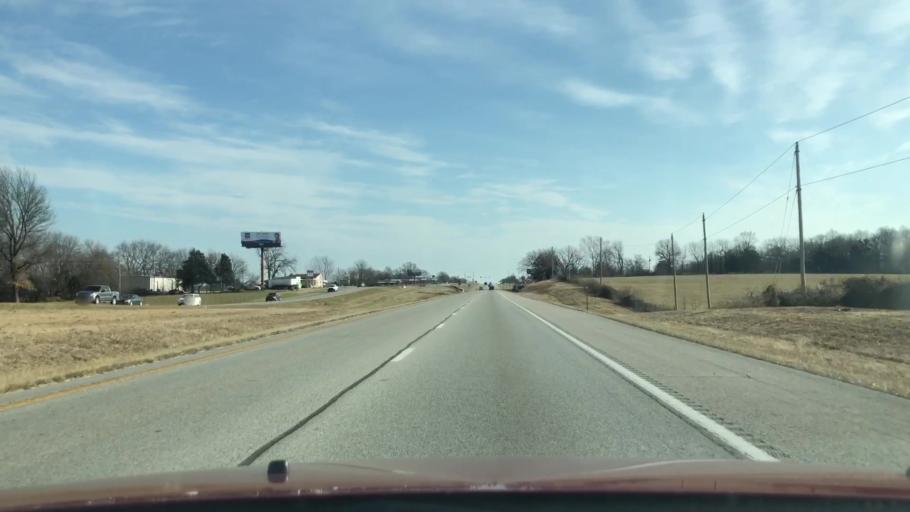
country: US
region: Missouri
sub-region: Webster County
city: Rogersville
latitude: 37.1188
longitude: -93.1278
